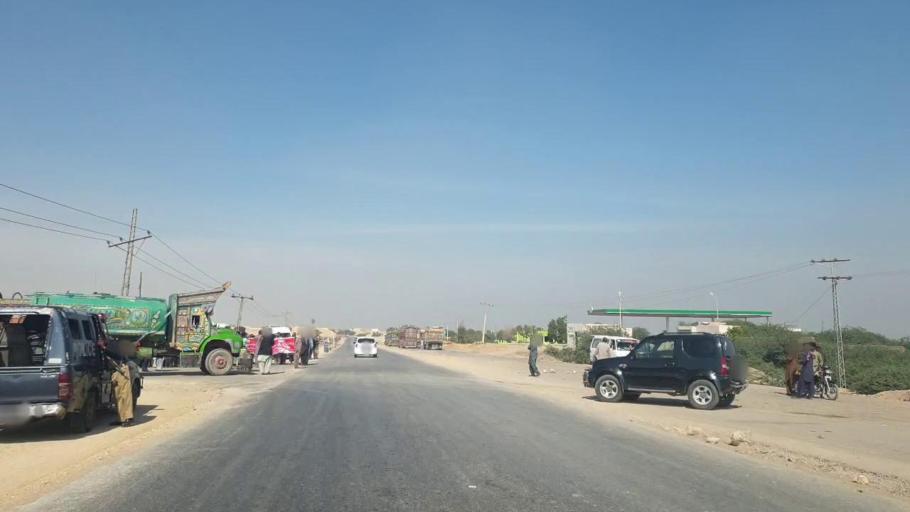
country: PK
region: Sindh
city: Hala
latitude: 25.7265
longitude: 68.2929
